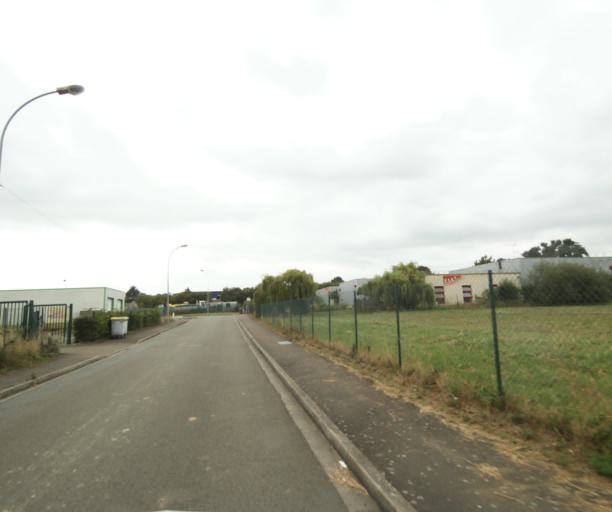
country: FR
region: Pays de la Loire
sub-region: Departement de la Sarthe
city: Solesmes
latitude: 47.8365
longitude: -0.3052
